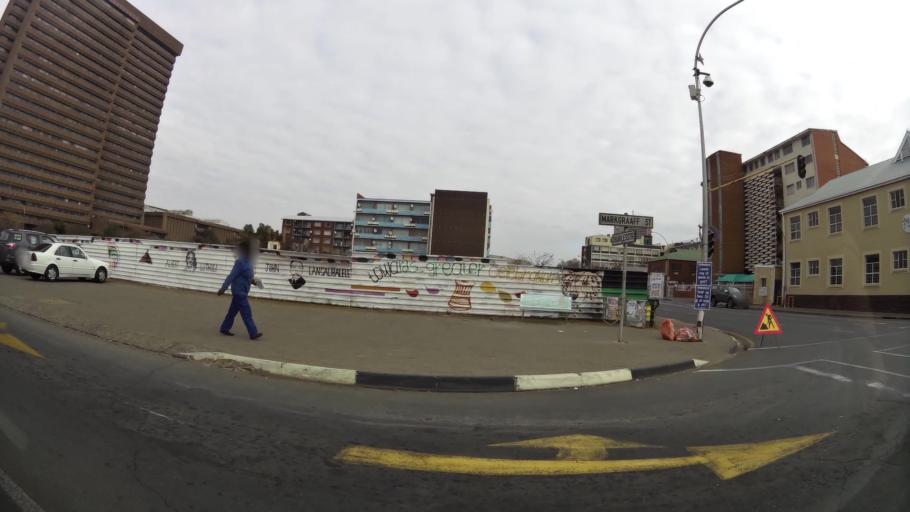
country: ZA
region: Orange Free State
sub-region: Mangaung Metropolitan Municipality
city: Bloemfontein
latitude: -29.1146
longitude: 26.2144
